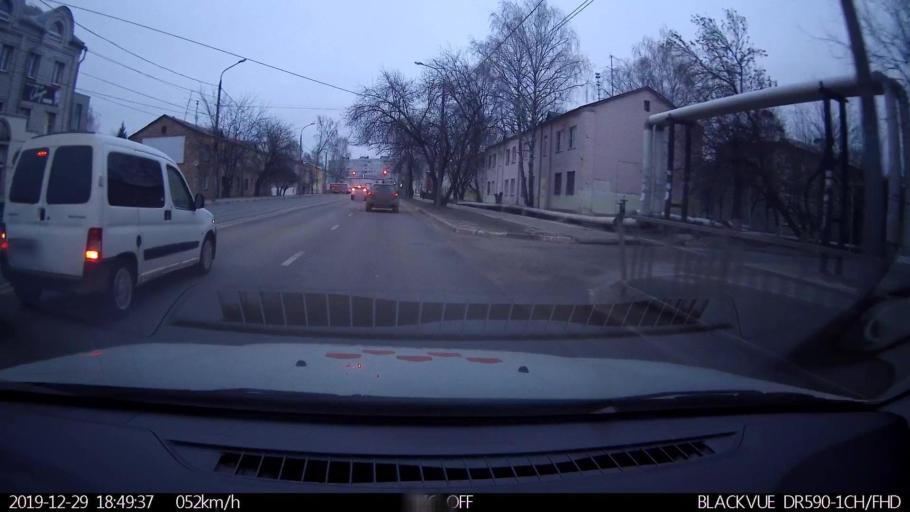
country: RU
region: Nizjnij Novgorod
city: Gorbatovka
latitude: 56.3466
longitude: 43.8446
